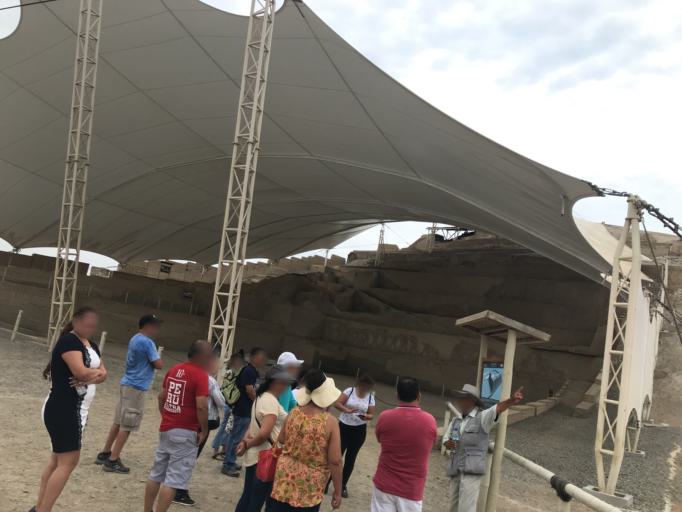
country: PE
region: La Libertad
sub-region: Ascope
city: Santiago de Cao
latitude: -7.9144
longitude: -79.3033
